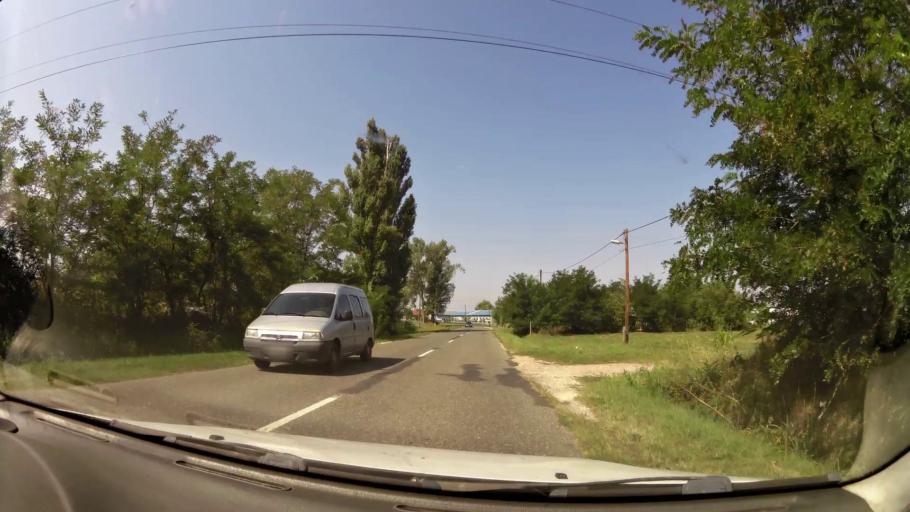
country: HU
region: Pest
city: Tapioszolos
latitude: 47.2829
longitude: 19.8702
